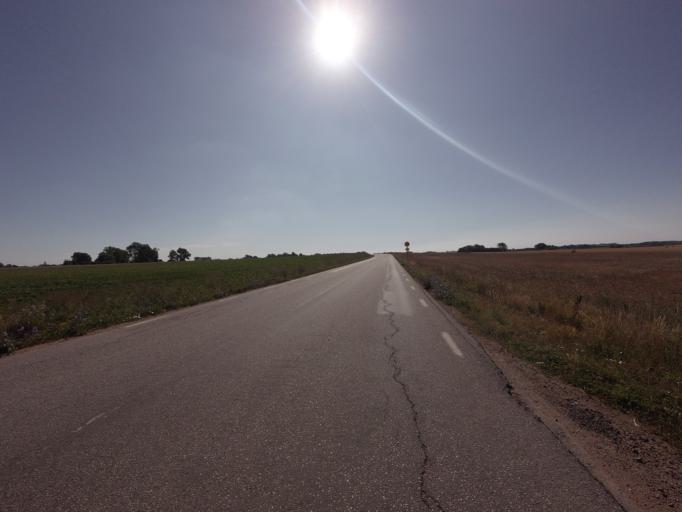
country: SE
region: Skane
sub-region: Trelleborgs Kommun
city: Skare
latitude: 55.4016
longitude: 13.0854
